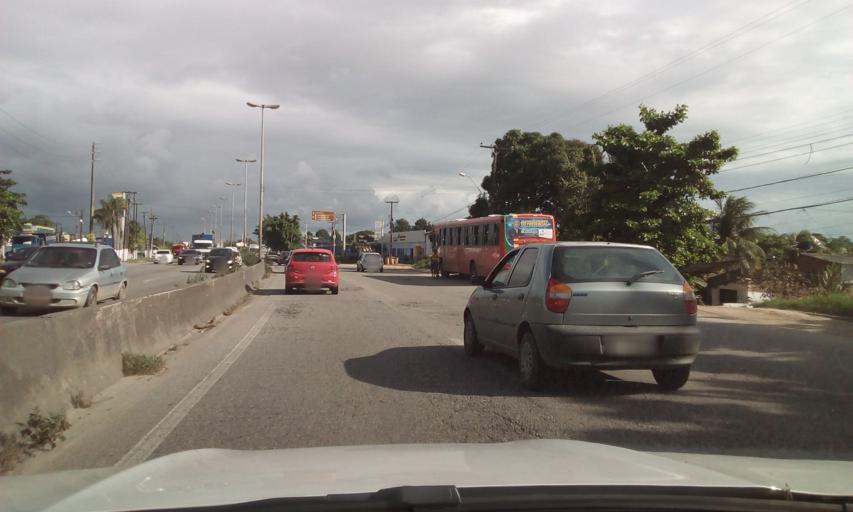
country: BR
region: Pernambuco
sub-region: Recife
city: Recife
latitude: -8.0198
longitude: -34.9425
